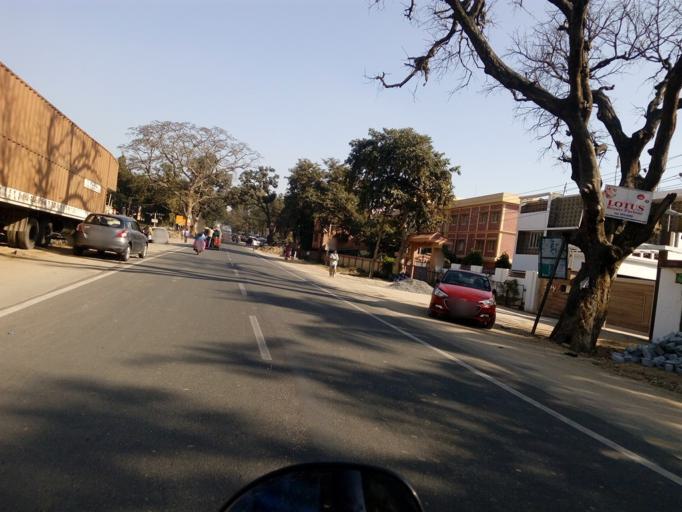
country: IN
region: Jharkhand
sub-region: Ranchi
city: Ranchi
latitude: 23.3599
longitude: 85.3575
